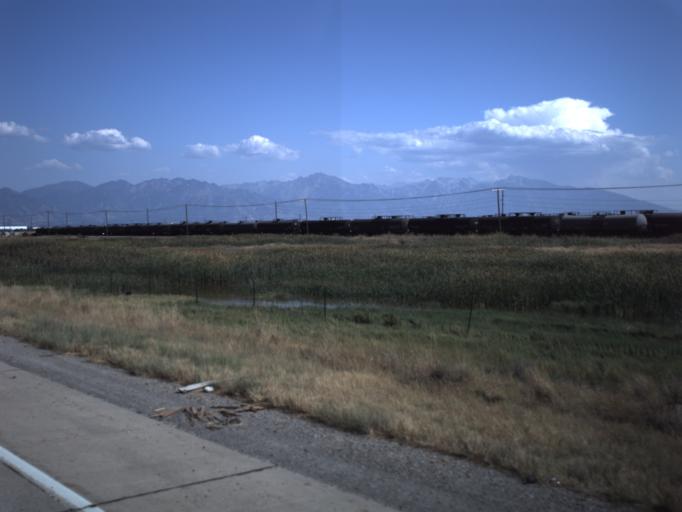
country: US
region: Utah
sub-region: Salt Lake County
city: Magna
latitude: 40.7708
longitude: -112.0558
